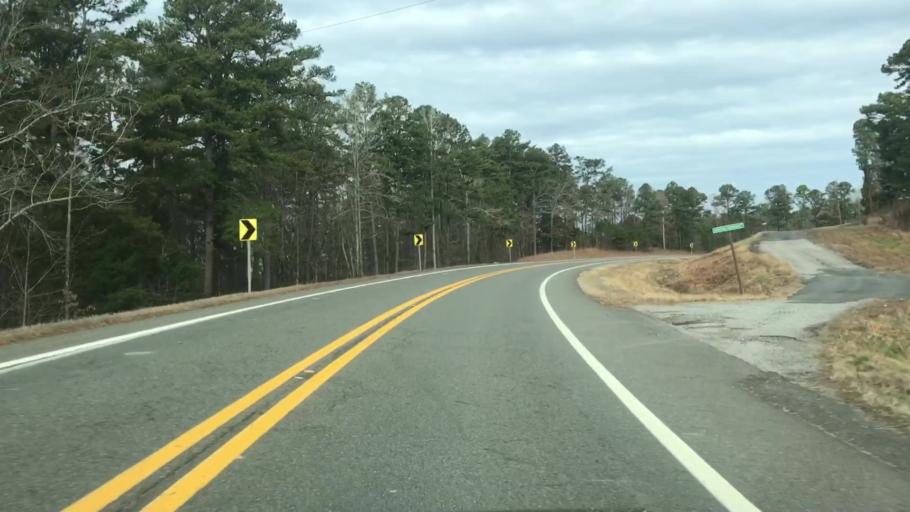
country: US
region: Arkansas
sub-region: Montgomery County
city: Mount Ida
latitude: 34.6123
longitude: -93.7028
